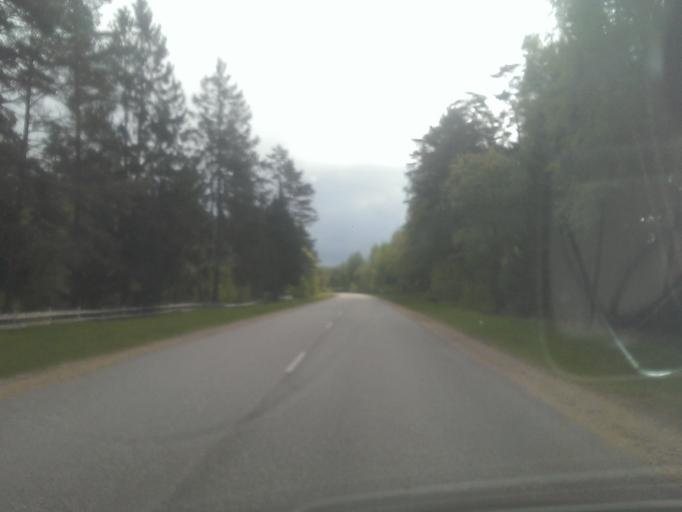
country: LV
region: Ventspils Rajons
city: Piltene
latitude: 57.1816
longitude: 21.6502
